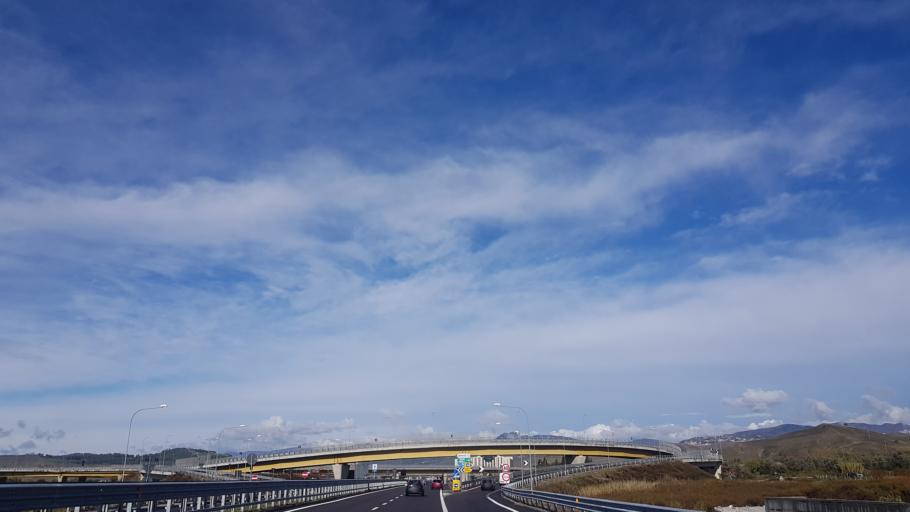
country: IT
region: Calabria
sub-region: Provincia di Catanzaro
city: Catanzaro
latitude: 38.8483
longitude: 16.5805
